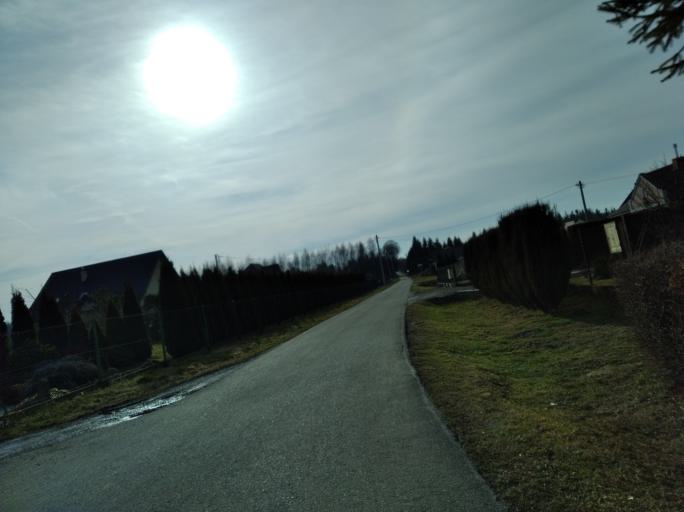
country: PL
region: Subcarpathian Voivodeship
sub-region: Powiat brzozowski
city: Grabownica Starzenska
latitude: 49.6482
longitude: 22.0707
